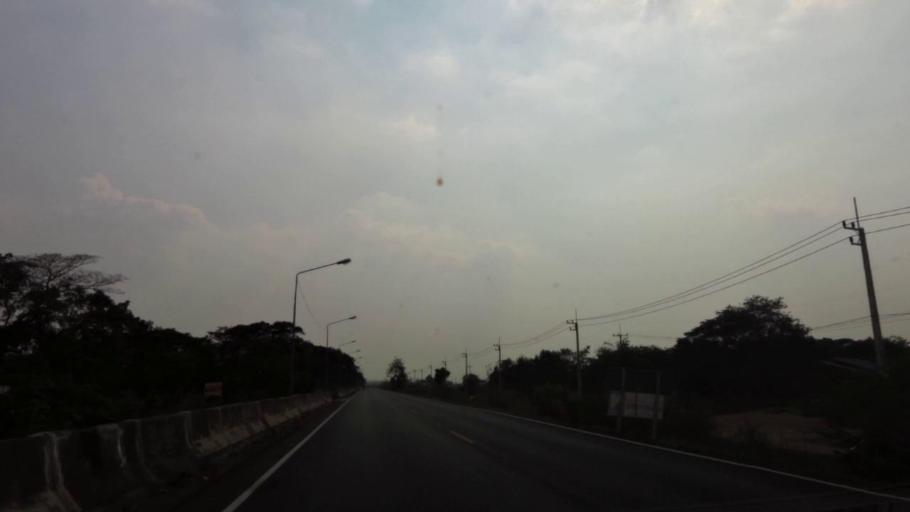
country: TH
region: Phra Nakhon Si Ayutthaya
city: Phra Nakhon Si Ayutthaya
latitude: 14.3095
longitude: 100.5634
